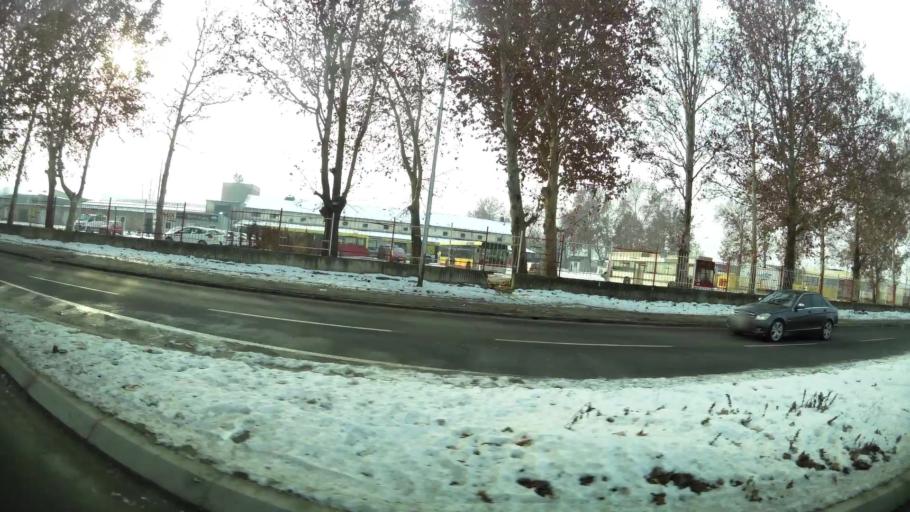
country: MK
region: Cair
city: Cair
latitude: 42.0252
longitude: 21.4308
